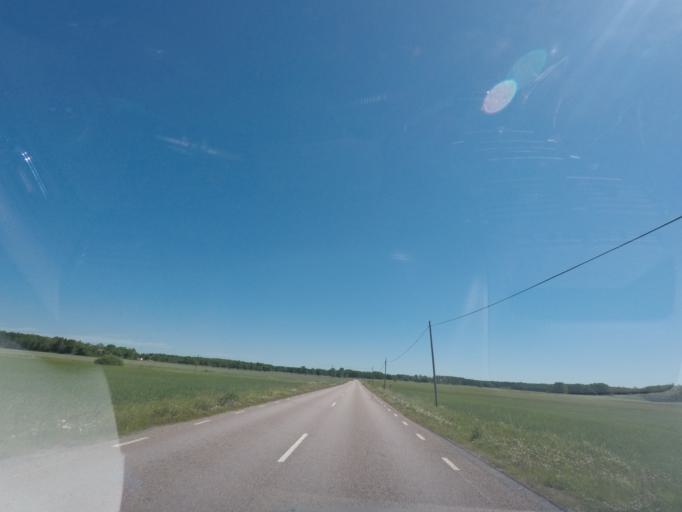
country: SE
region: Vaestmanland
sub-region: Vasteras
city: Tillberga
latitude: 59.6807
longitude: 16.7664
